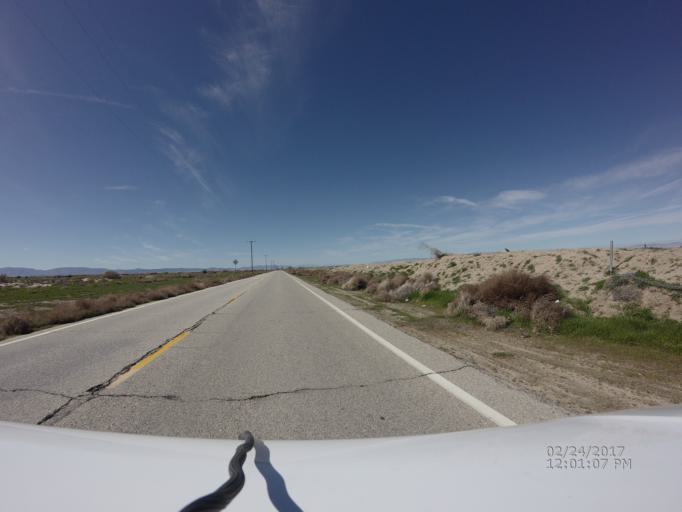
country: US
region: California
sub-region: Los Angeles County
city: Lancaster
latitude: 34.7192
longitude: -118.0246
